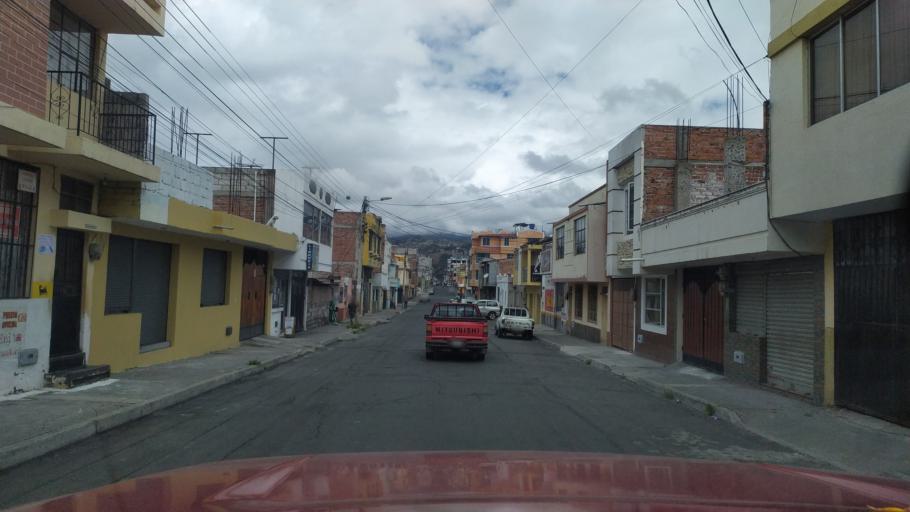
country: EC
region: Chimborazo
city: Riobamba
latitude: -1.6684
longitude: -78.6423
